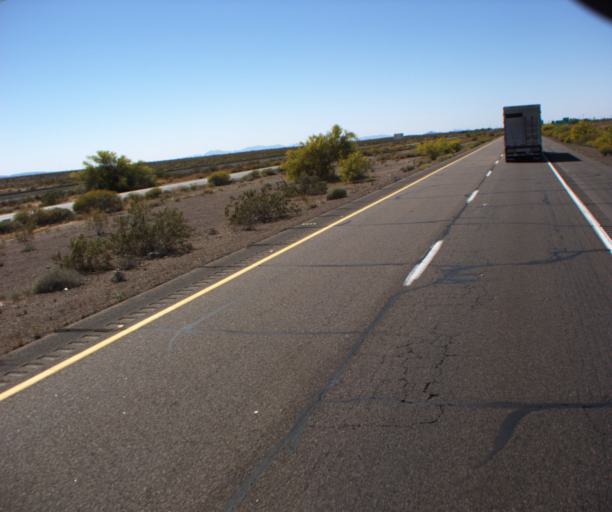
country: US
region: Arizona
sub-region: Maricopa County
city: Gila Bend
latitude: 32.8603
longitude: -113.1945
